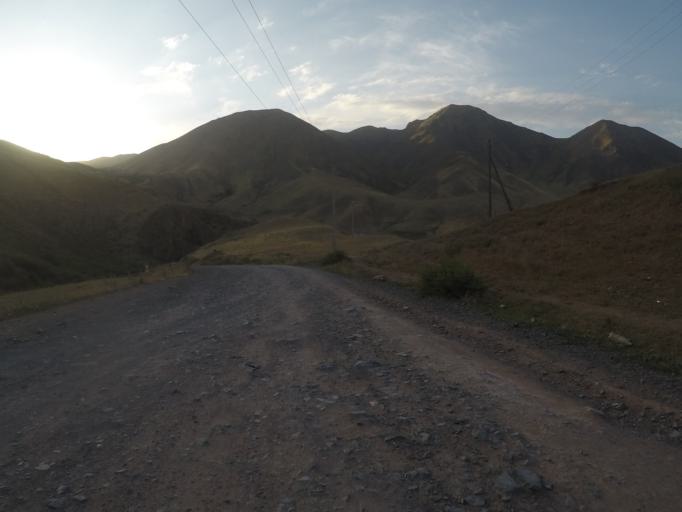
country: KG
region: Chuy
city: Bishkek
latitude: 42.6688
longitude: 74.6474
